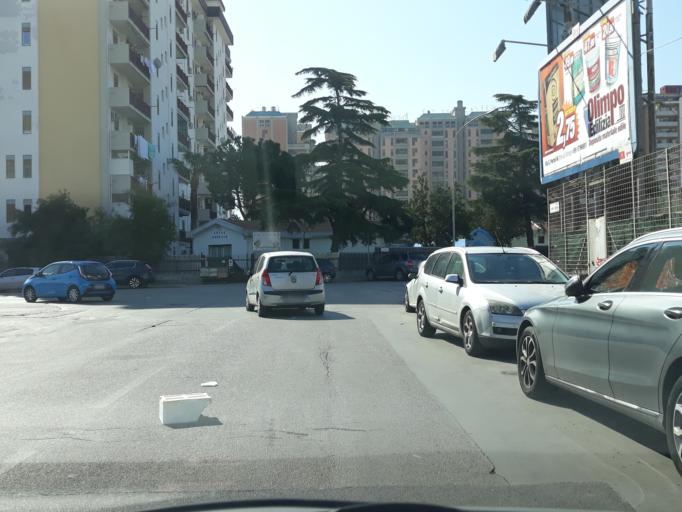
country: IT
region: Sicily
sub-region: Palermo
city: Palermo
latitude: 38.1327
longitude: 13.3333
